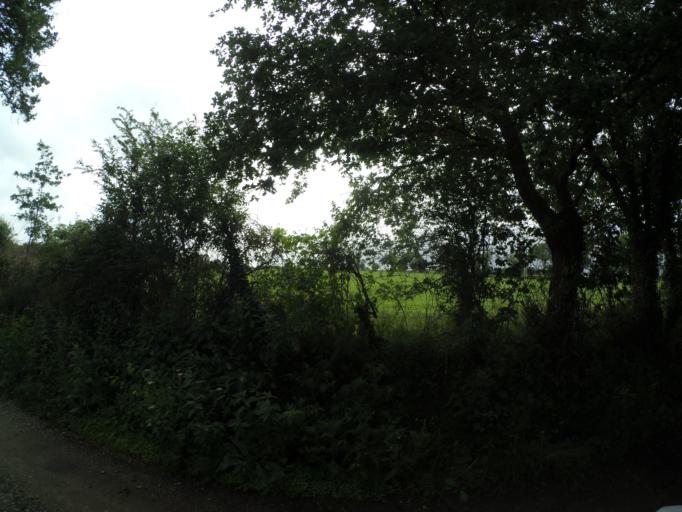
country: FR
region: Pays de la Loire
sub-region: Departement de la Vendee
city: Nesmy
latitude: 46.6106
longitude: -1.3960
